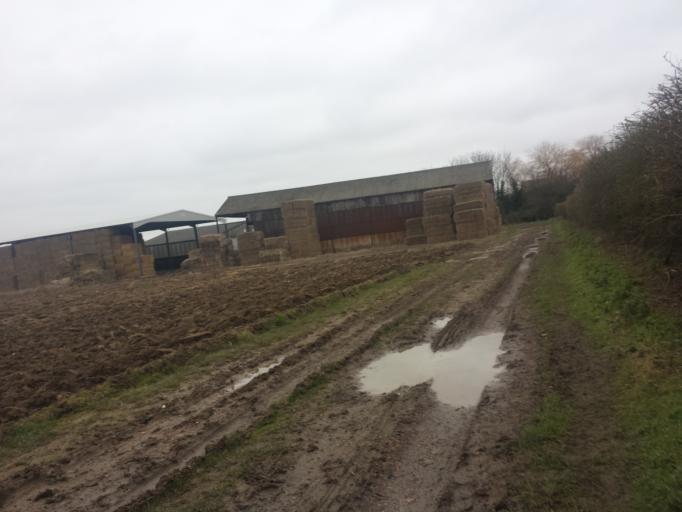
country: GB
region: England
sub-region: Essex
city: Little Clacton
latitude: 51.8682
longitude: 1.1618
